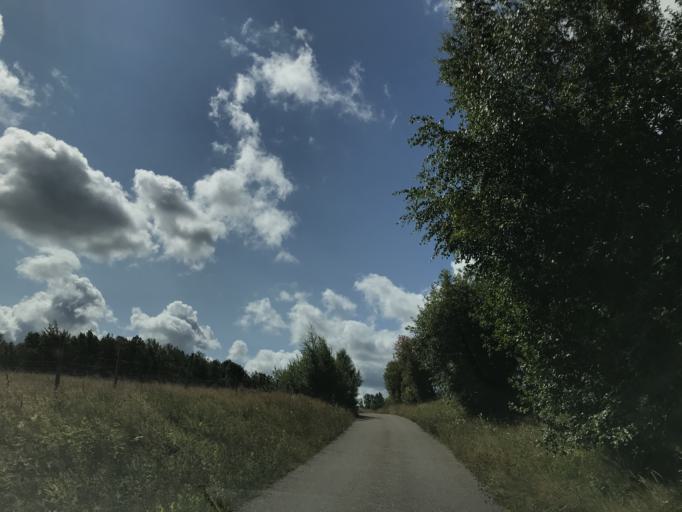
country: SE
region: Halland
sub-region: Laholms Kommun
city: Knared
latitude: 56.5144
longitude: 13.3021
